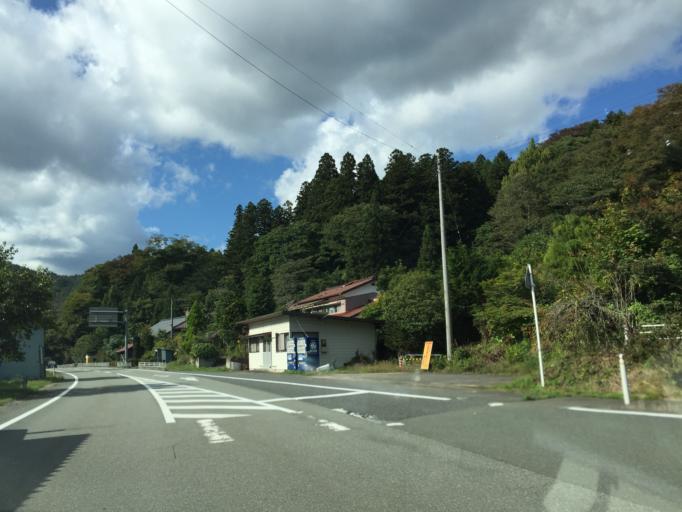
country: JP
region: Fukushima
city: Namie
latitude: 37.5417
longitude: 140.8616
